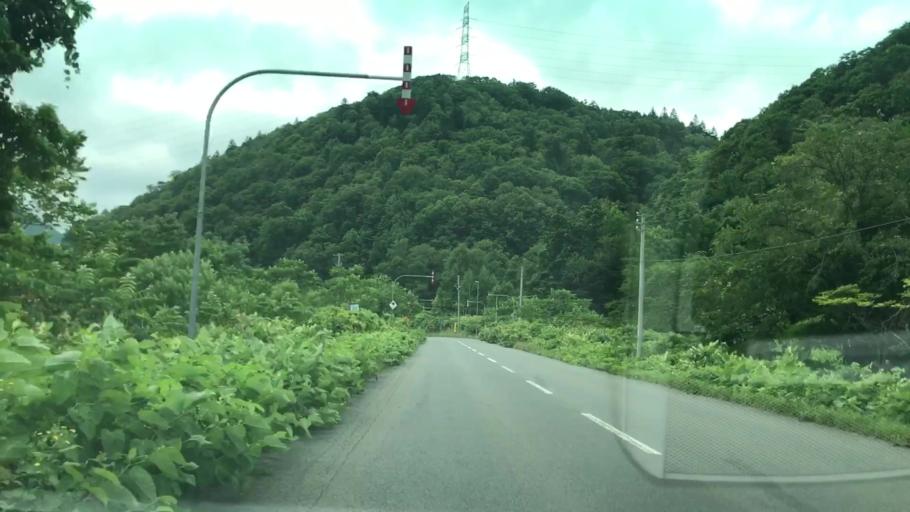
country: JP
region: Hokkaido
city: Yoichi
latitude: 43.0405
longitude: 140.8598
